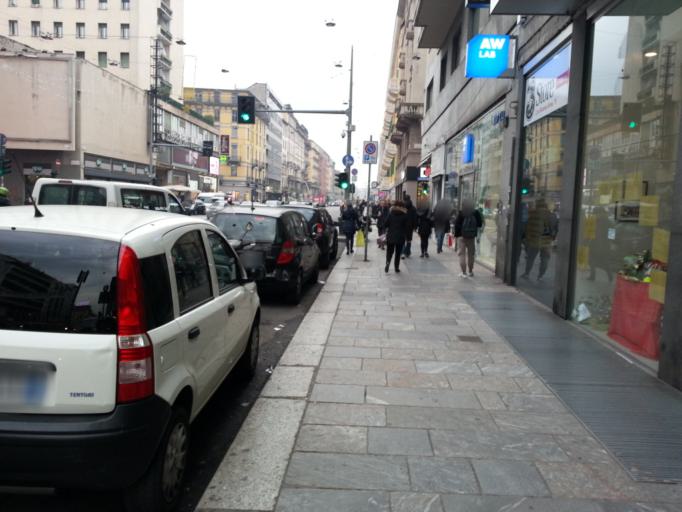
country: IT
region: Lombardy
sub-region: Citta metropolitana di Milano
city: Milano
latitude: 45.4793
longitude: 9.2102
